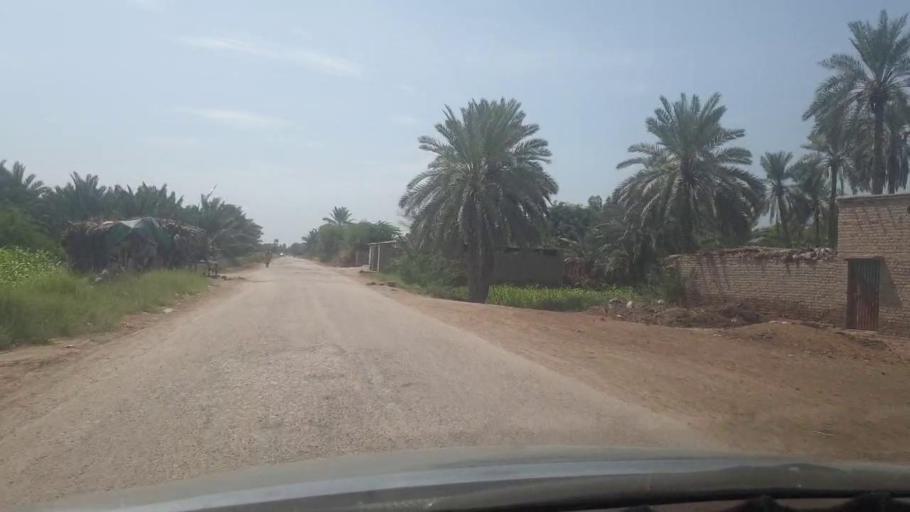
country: PK
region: Sindh
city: Bozdar
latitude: 27.2059
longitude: 68.5800
